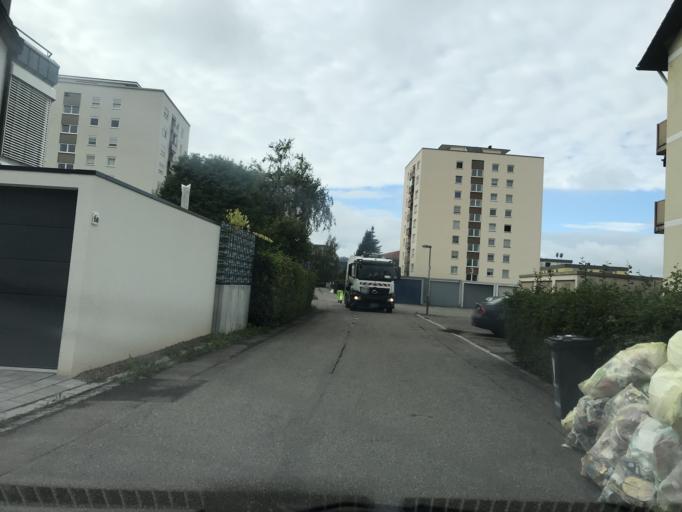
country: DE
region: Baden-Wuerttemberg
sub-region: Freiburg Region
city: Schopfheim
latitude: 47.6560
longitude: 7.8380
